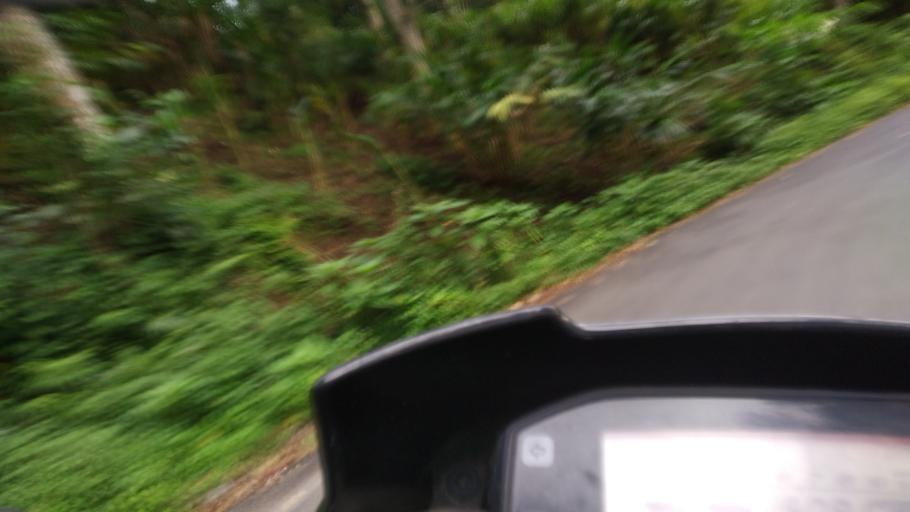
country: IN
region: Tamil Nadu
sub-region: Theni
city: Bodinayakkanur
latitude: 10.0325
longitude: 77.2301
